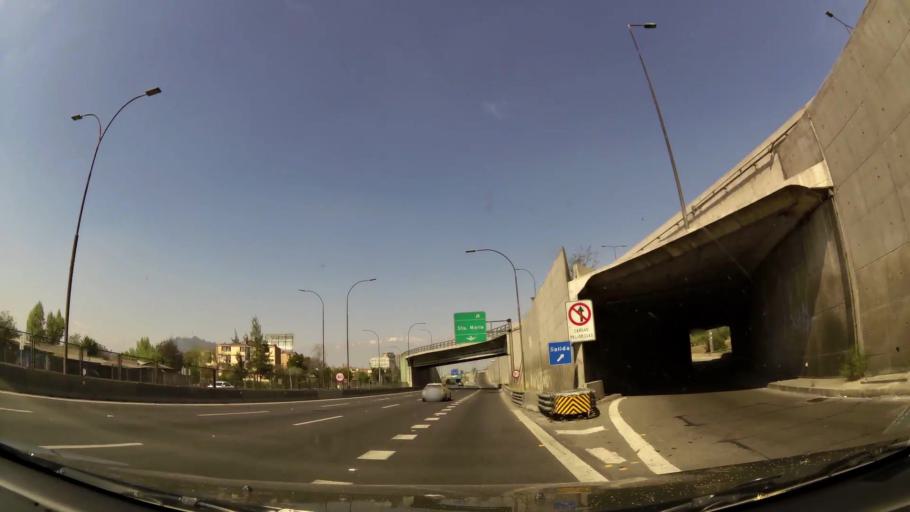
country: CL
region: Santiago Metropolitan
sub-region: Provincia de Santiago
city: Santiago
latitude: -33.4271
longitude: -70.6675
